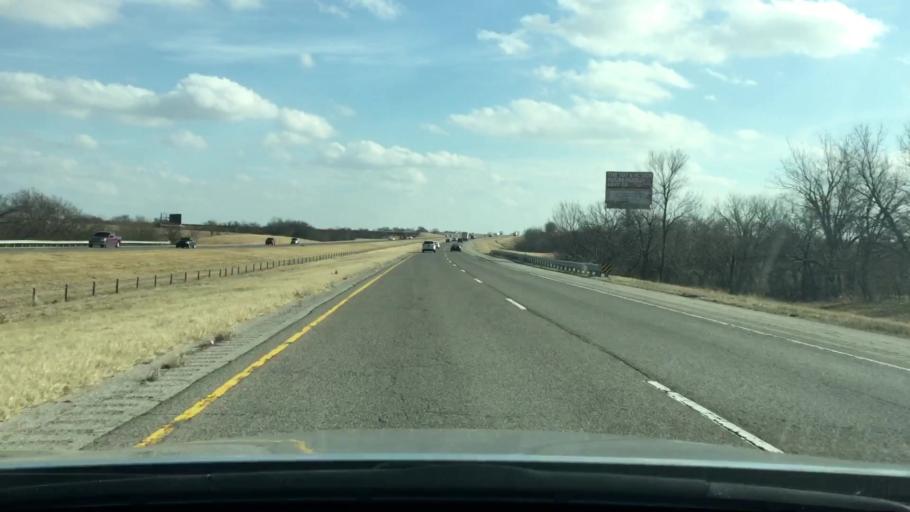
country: US
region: Oklahoma
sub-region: Garvin County
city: Maysville
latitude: 34.8947
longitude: -97.3433
